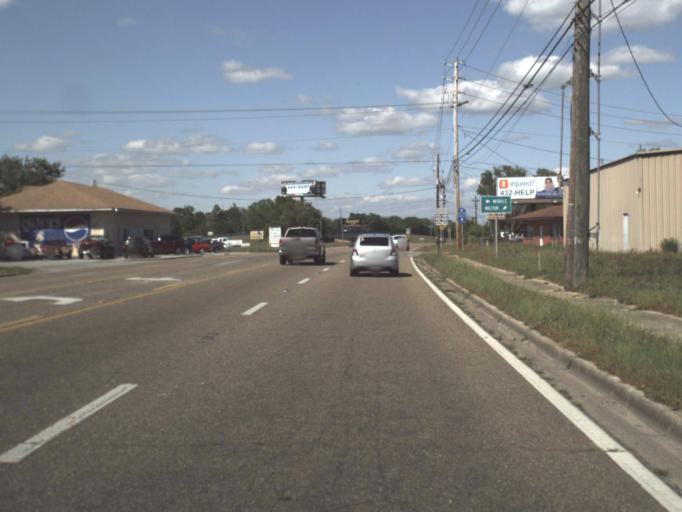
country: US
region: Florida
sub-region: Escambia County
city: Ferry Pass
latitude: 30.5311
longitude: -87.2074
